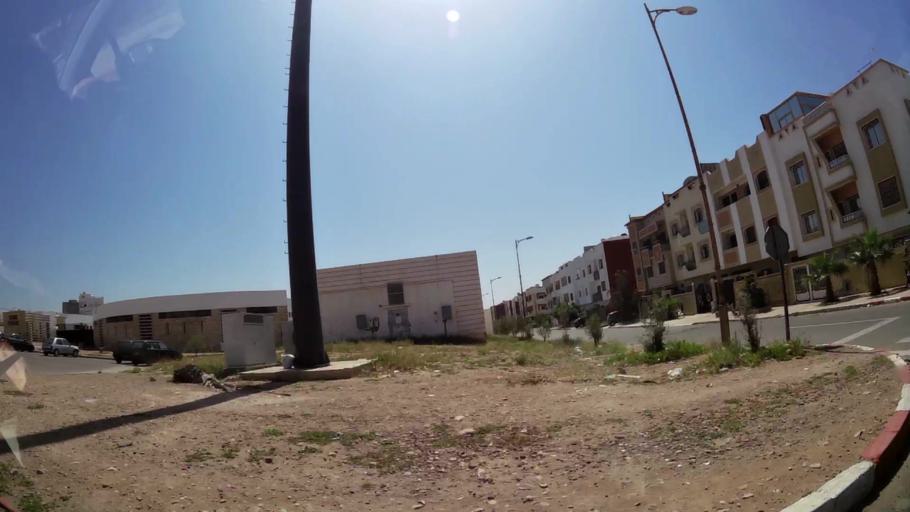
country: MA
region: Oued ed Dahab-Lagouira
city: Dakhla
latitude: 30.4308
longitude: -9.5610
